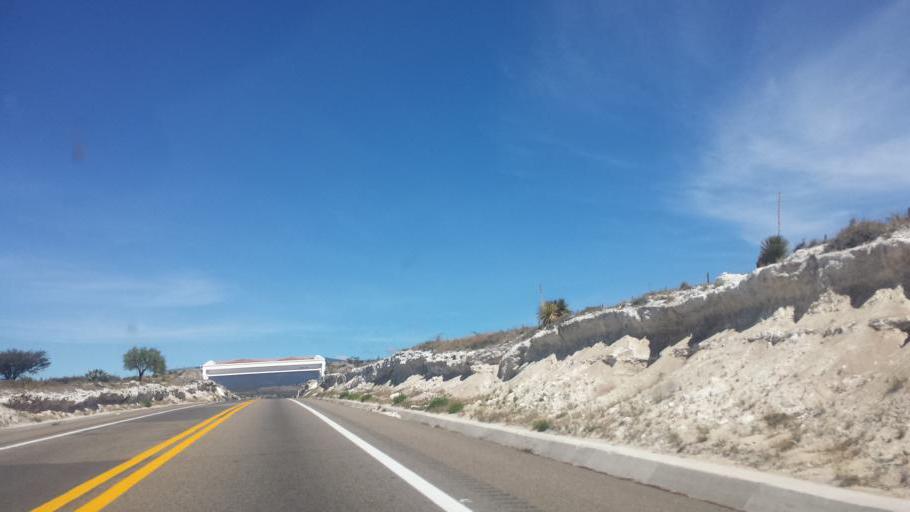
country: MX
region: Oaxaca
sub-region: Villa Tejupam de la Union
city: Villa Tejupam de la Union
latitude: 17.9159
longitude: -97.3618
